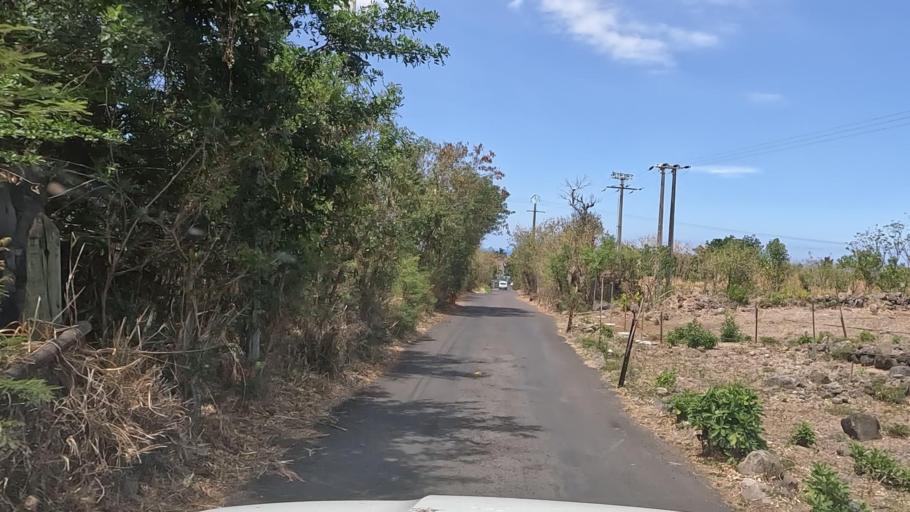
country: RE
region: Reunion
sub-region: Reunion
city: Saint-Louis
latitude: -21.2789
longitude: 55.4449
